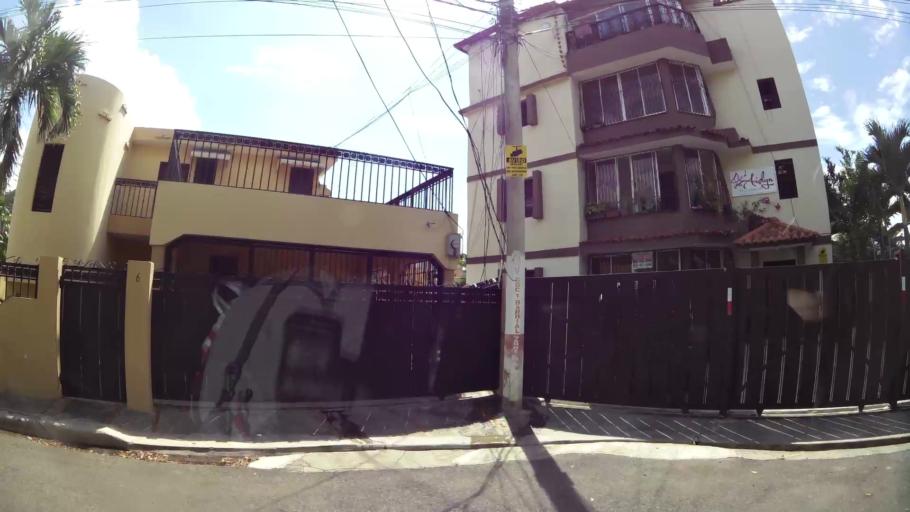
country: DO
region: Santiago
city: Santiago de los Caballeros
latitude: 19.4735
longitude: -70.6977
